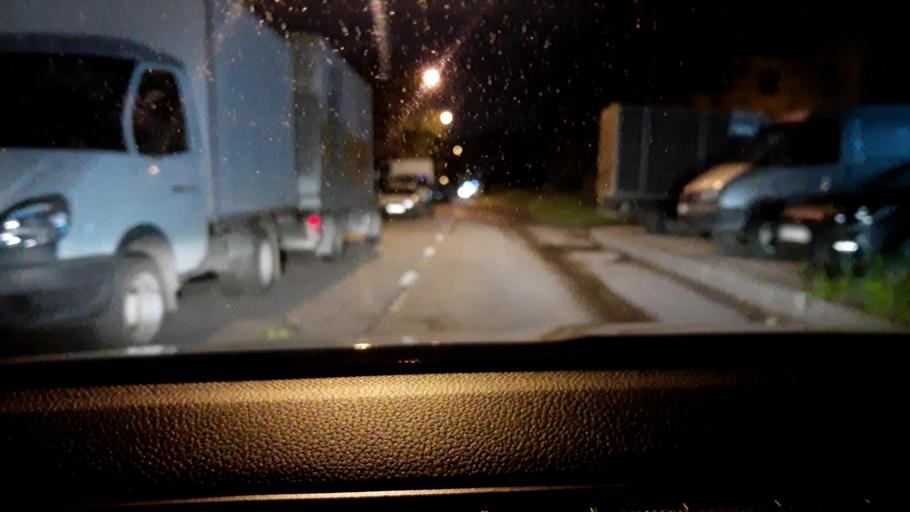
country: RU
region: Moskovskaya
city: Korolev
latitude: 55.9070
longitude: 37.8457
